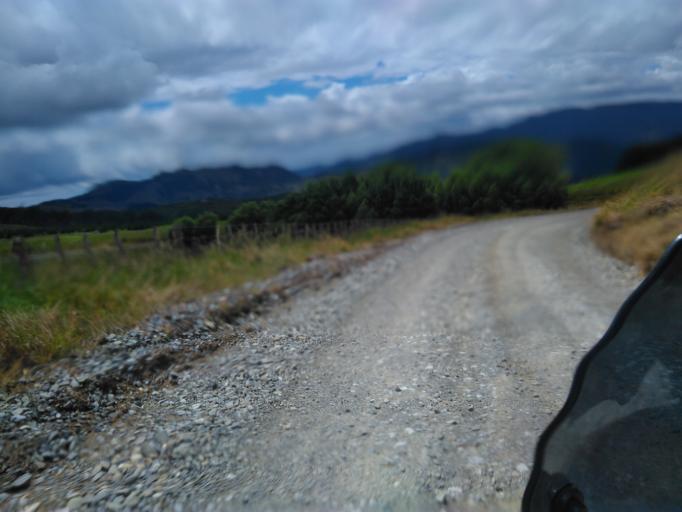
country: NZ
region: Gisborne
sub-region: Gisborne District
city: Gisborne
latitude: -38.1882
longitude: 178.0992
